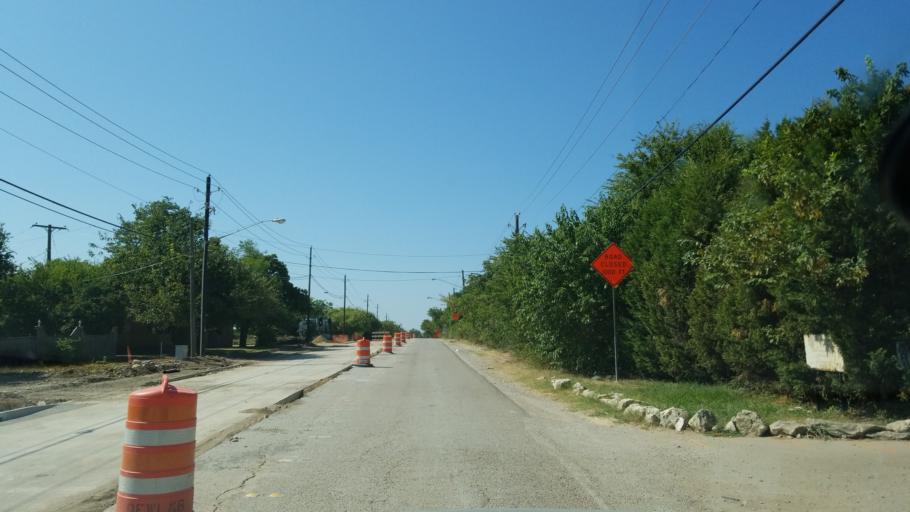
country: US
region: Texas
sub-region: Dallas County
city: Cockrell Hill
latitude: 32.7477
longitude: -96.8914
